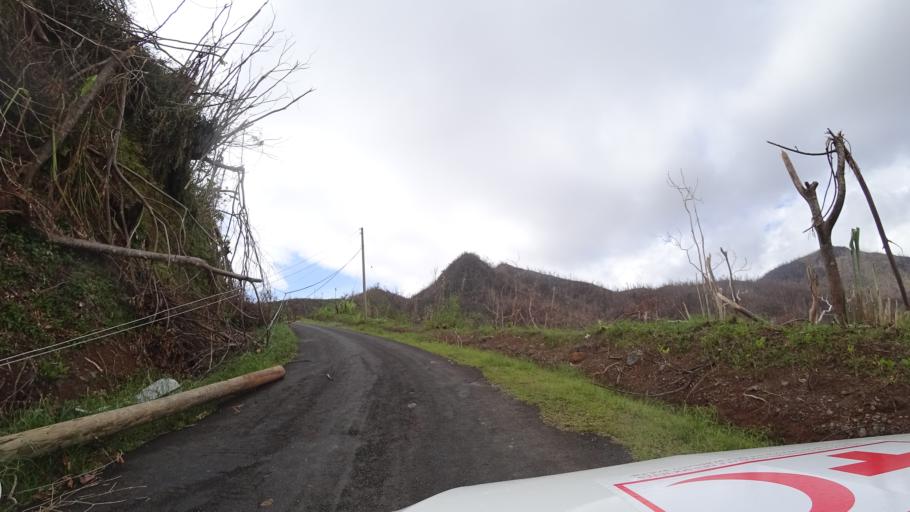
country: DM
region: Saint David
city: Rosalie
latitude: 15.3944
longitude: -61.2614
